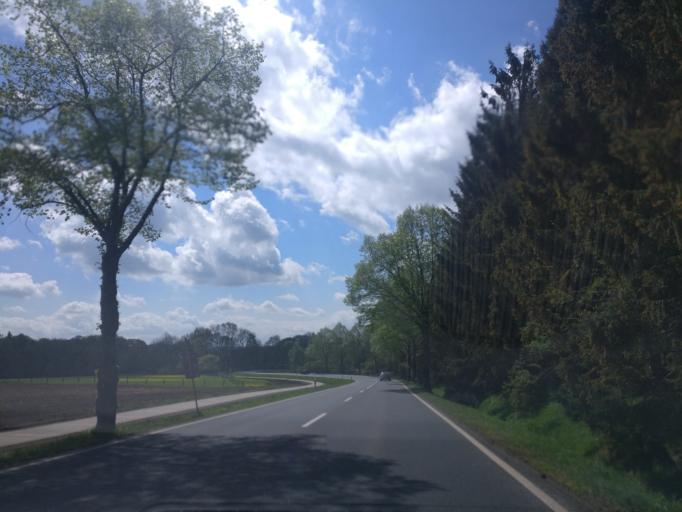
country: DE
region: Lower Saxony
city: Scheden
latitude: 51.4854
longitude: 9.7243
